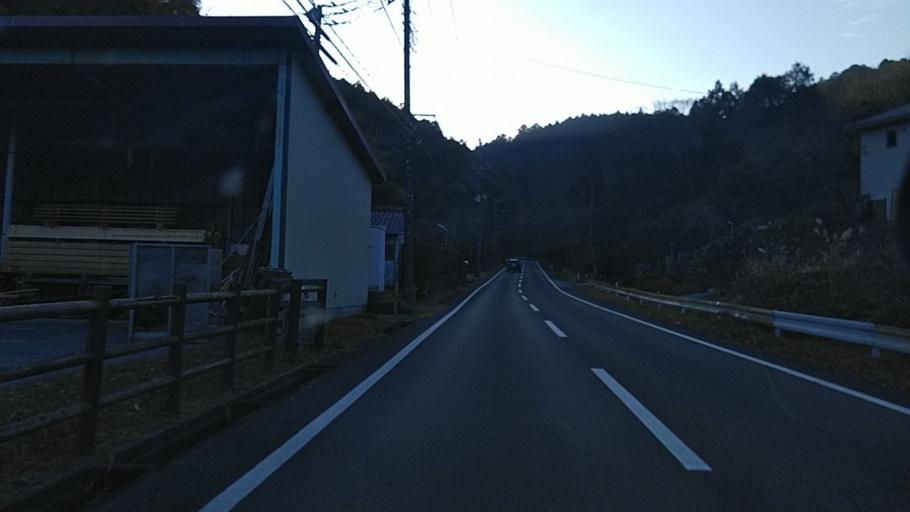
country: JP
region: Chiba
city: Kimitsu
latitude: 35.2689
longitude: 139.9229
